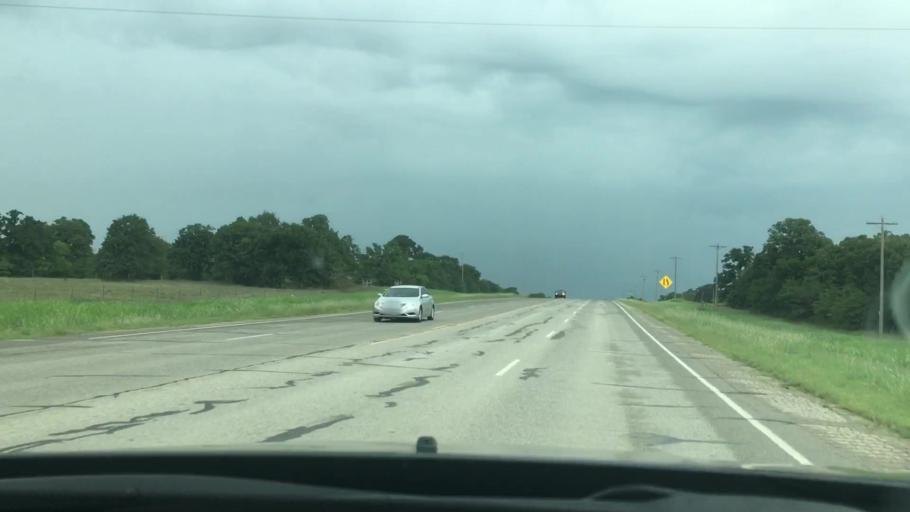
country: US
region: Oklahoma
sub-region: Carter County
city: Healdton
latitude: 34.1946
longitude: -97.4747
